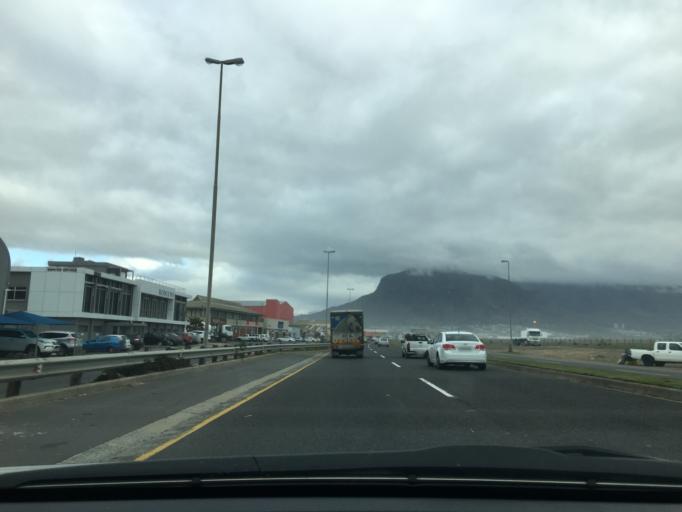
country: ZA
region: Western Cape
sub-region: City of Cape Town
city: Sunset Beach
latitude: -33.9032
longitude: 18.4767
